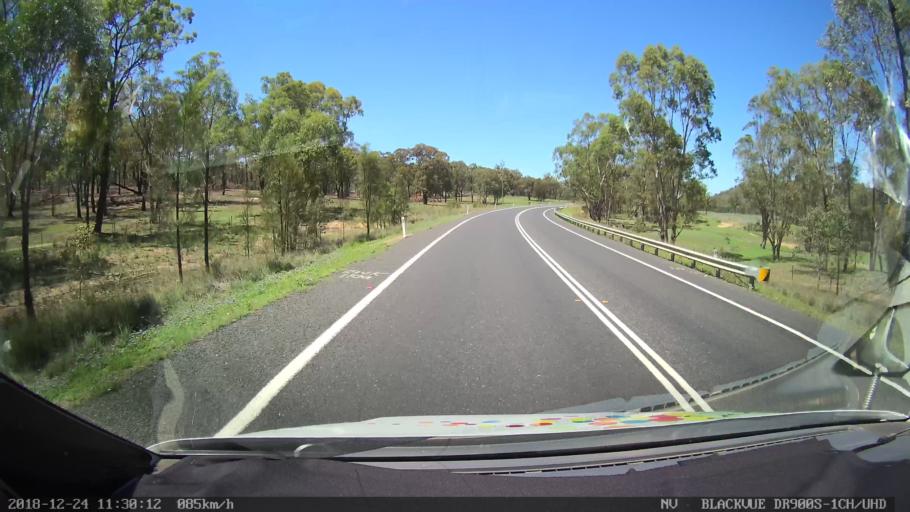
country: AU
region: New South Wales
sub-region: Upper Hunter Shire
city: Merriwa
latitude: -32.2019
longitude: 150.4675
